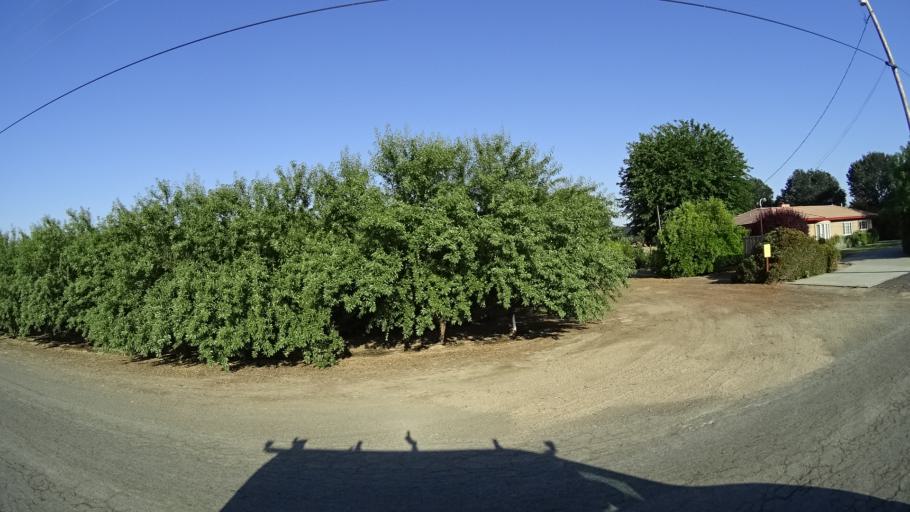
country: US
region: California
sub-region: Kings County
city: Lemoore
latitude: 36.2621
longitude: -119.7446
